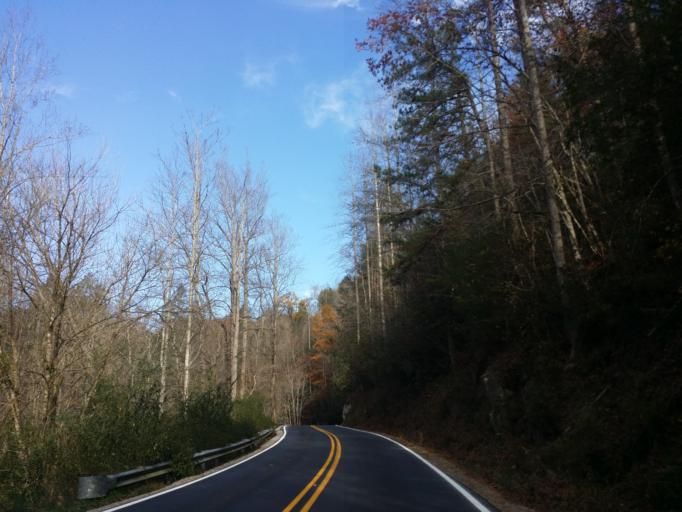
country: US
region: North Carolina
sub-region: McDowell County
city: Marion
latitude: 35.7294
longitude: -82.0934
